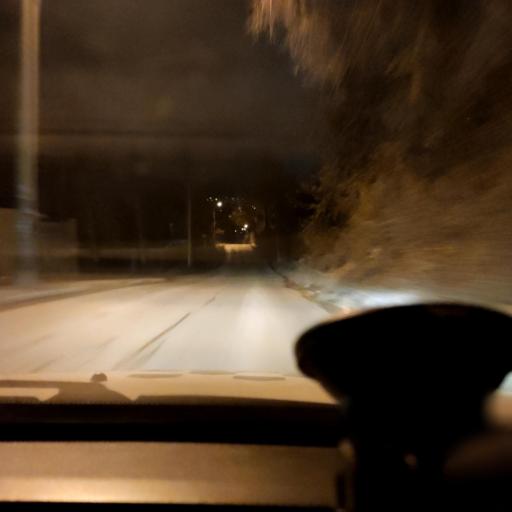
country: RU
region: Perm
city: Perm
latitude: 58.0319
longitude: 56.3131
